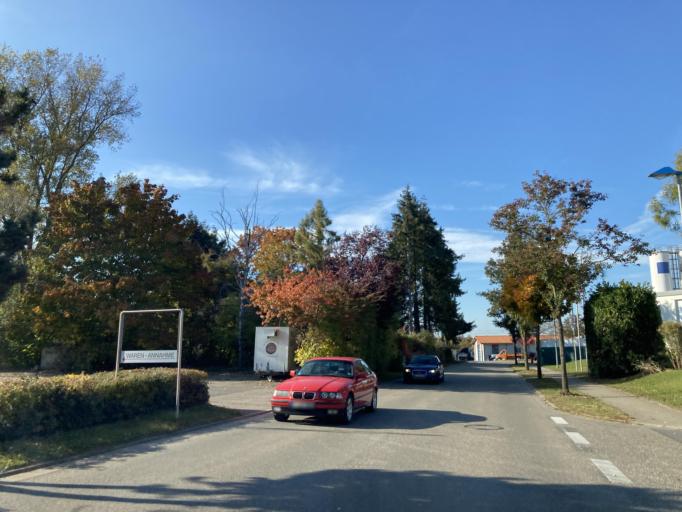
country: DE
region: Baden-Wuerttemberg
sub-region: Freiburg Region
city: Heitersheim
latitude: 47.8755
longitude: 7.6462
